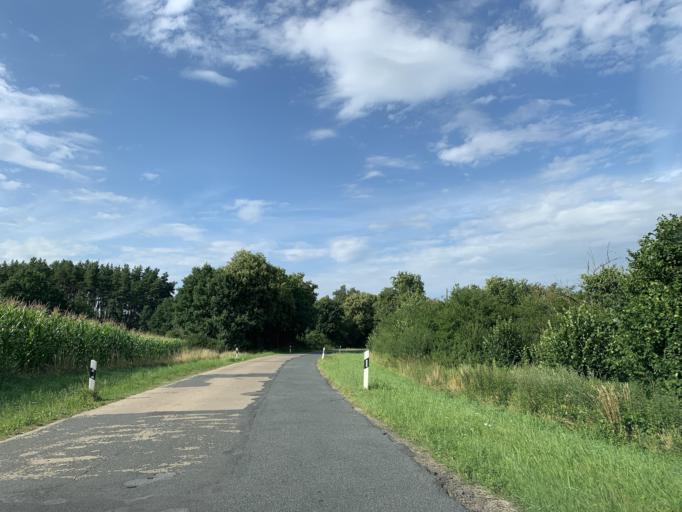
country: DE
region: Mecklenburg-Vorpommern
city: Carpin
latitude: 53.3730
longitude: 13.1777
